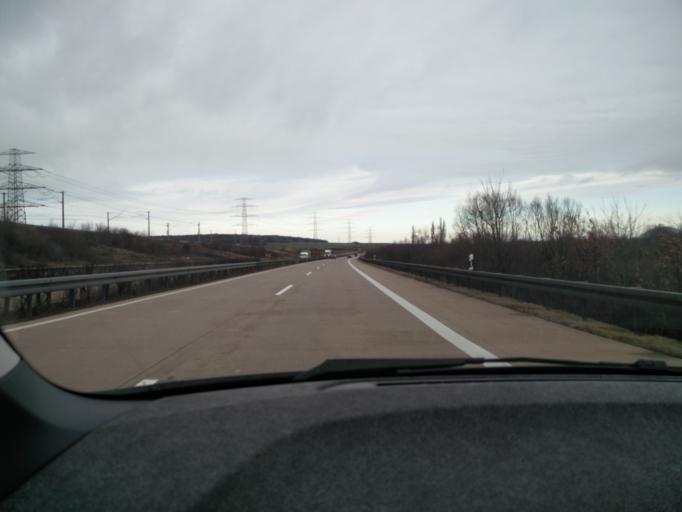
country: DE
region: Thuringia
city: Behringen
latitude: 50.7972
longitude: 11.0005
